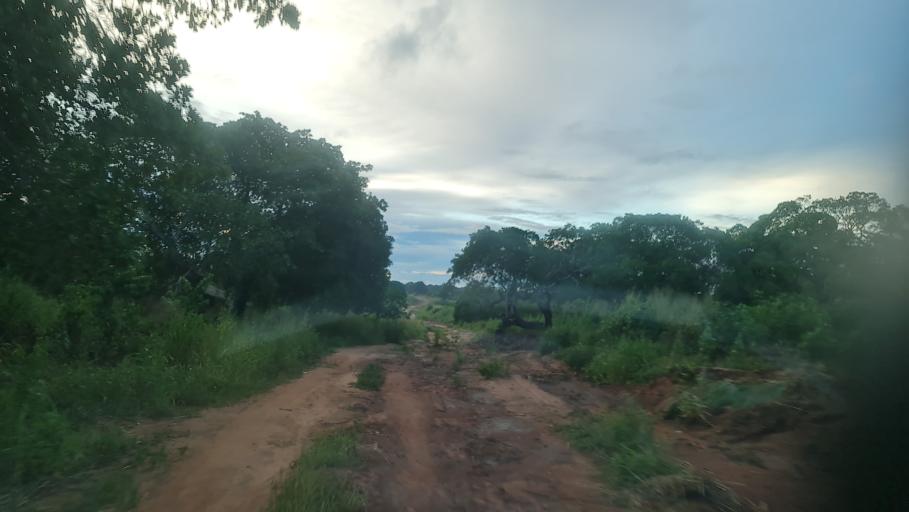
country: MZ
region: Nampula
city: Nampula
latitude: -14.7394
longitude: 39.9322
